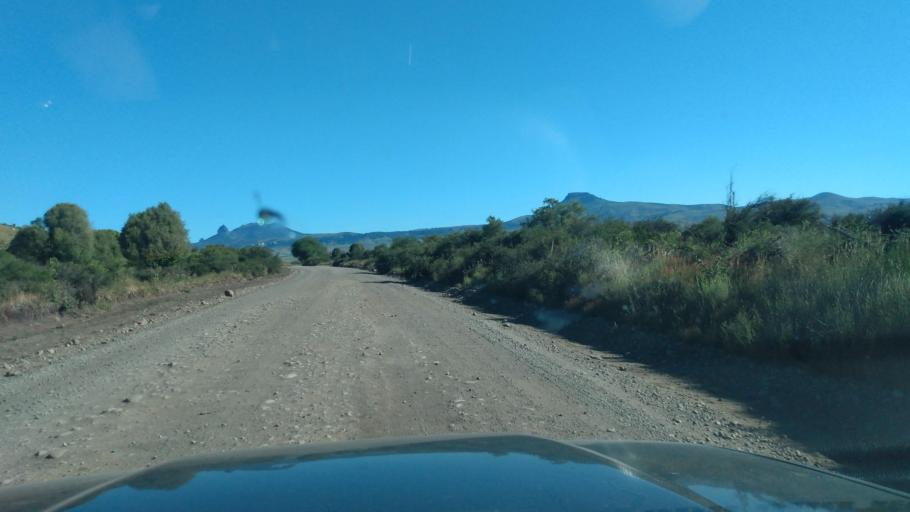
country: AR
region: Neuquen
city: Junin de los Andes
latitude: -39.8419
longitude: -71.1886
